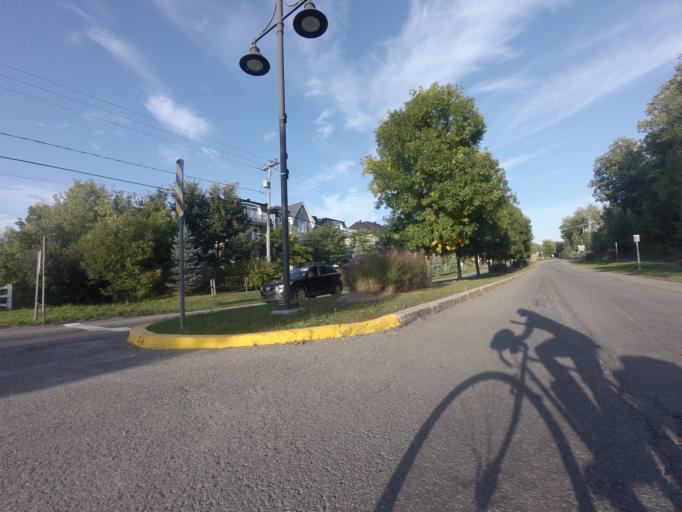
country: CA
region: Quebec
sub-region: Laurentides
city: Prevost
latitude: 45.8407
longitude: -74.0595
